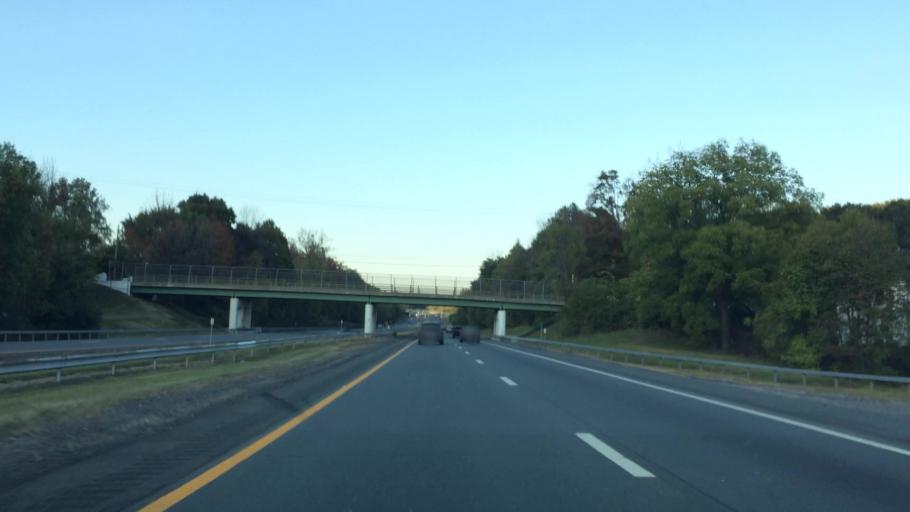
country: US
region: New York
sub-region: Orange County
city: Woodbury
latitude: 41.4055
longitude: -74.0811
